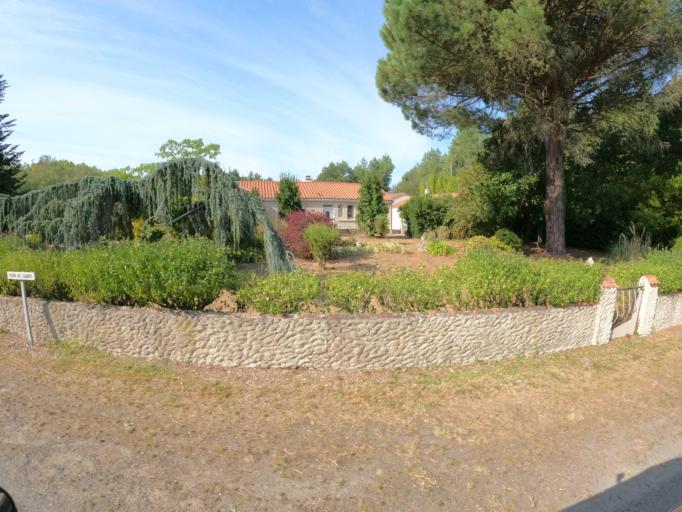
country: FR
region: Pays de la Loire
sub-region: Departement de la Vendee
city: Saint-Christophe-du-Ligneron
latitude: 46.8024
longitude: -1.7960
